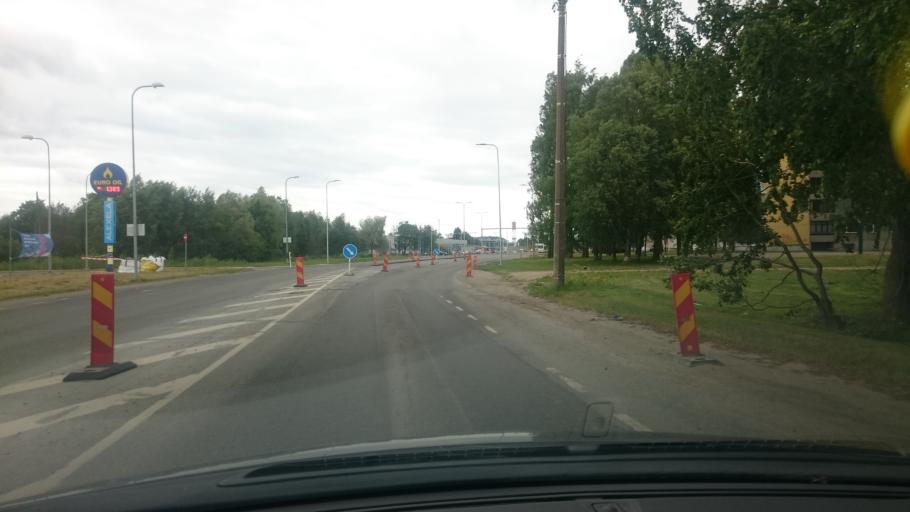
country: EE
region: Harju
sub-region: Saue vald
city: Laagri
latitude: 59.4188
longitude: 24.6381
